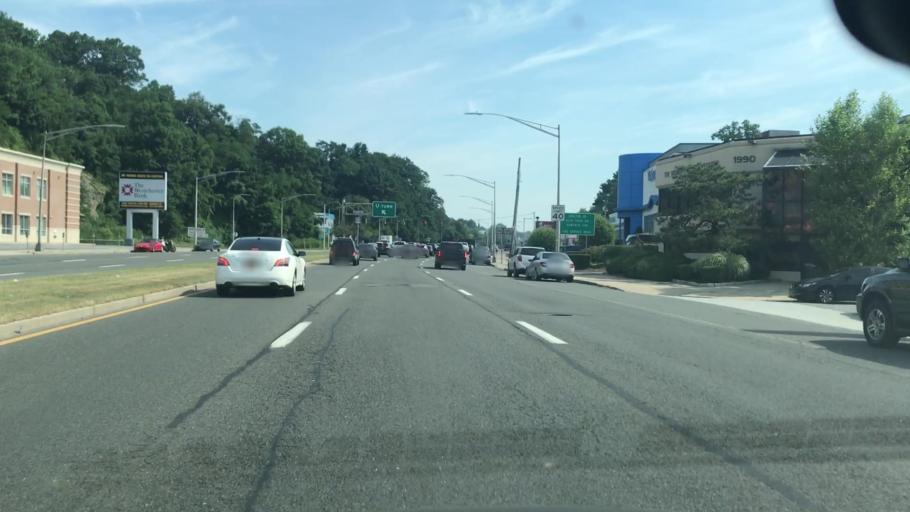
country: US
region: New York
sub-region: Westchester County
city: Tuckahoe
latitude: 40.9660
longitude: -73.8382
